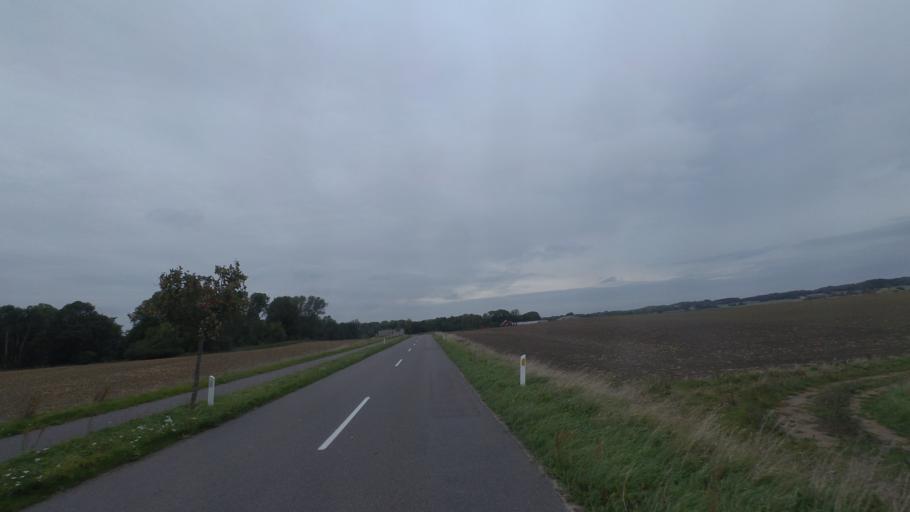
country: DK
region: Capital Region
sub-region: Bornholm Kommune
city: Akirkeby
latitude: 55.0052
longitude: 14.9981
